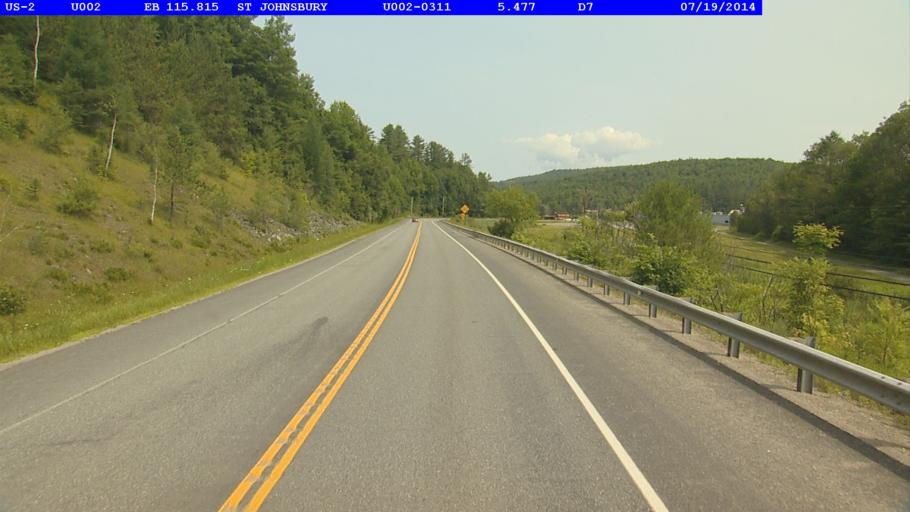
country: US
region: Vermont
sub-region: Caledonia County
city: St Johnsbury
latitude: 44.4241
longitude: -71.9802
